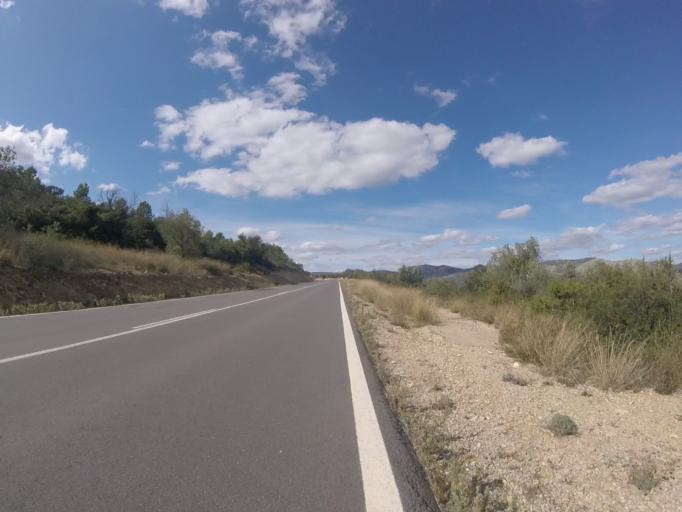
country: ES
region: Valencia
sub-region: Provincia de Castello
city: Chert/Xert
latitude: 40.4380
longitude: 0.1252
